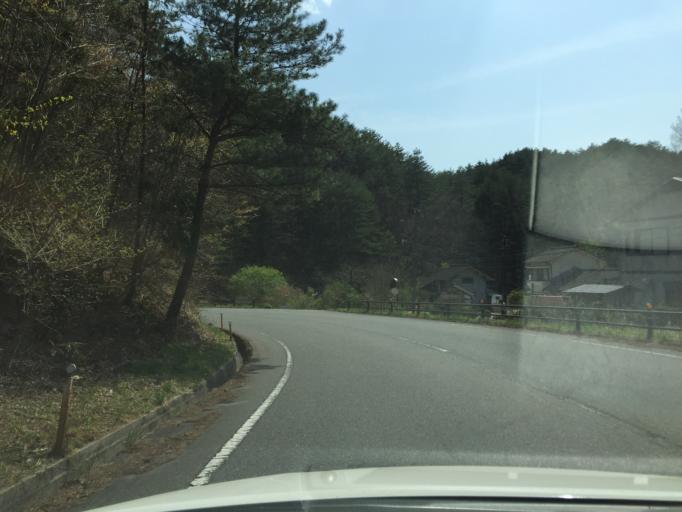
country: JP
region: Fukushima
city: Namie
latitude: 37.3720
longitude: 140.8020
